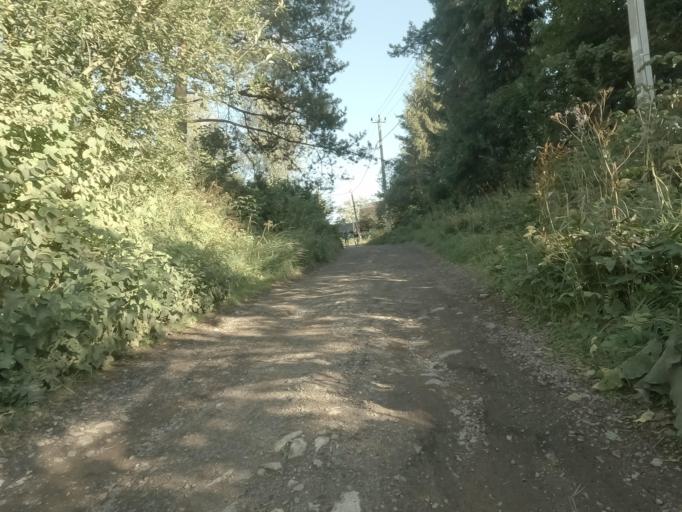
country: RU
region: Leningrad
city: Kirovsk
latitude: 59.9250
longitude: 30.9796
